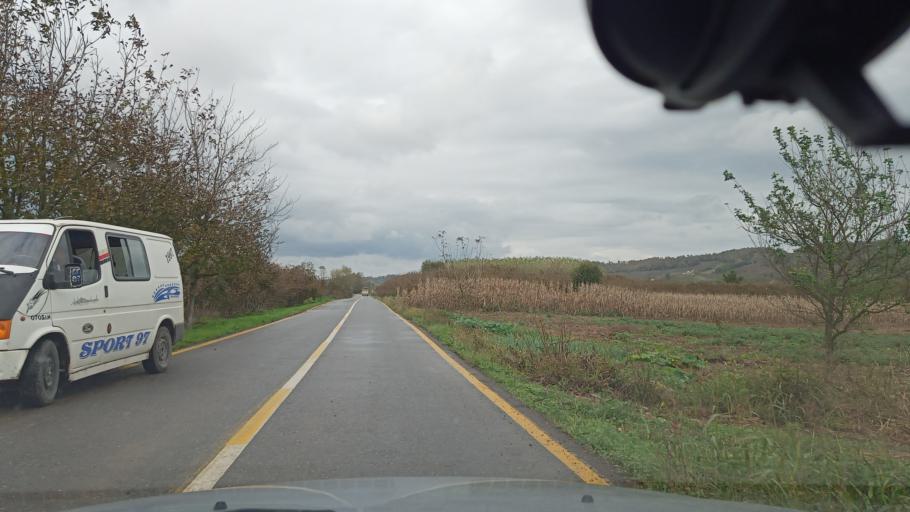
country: TR
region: Sakarya
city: Karasu
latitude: 41.0516
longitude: 30.6042
